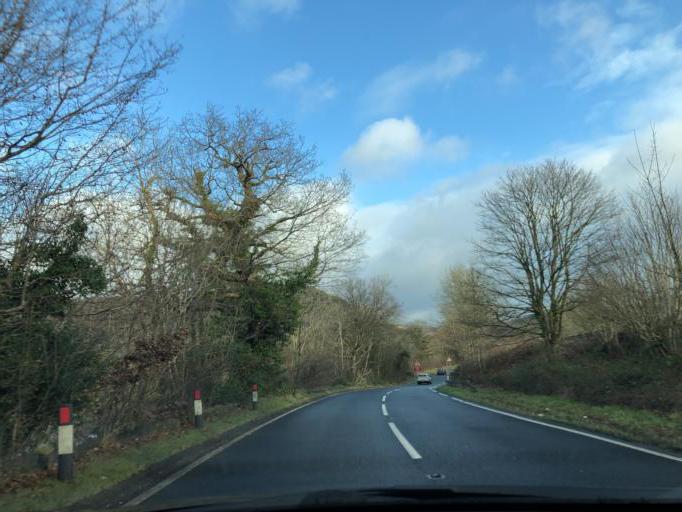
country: GB
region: England
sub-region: Cumbria
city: Grange-over-Sands
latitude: 54.2666
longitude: -2.9784
